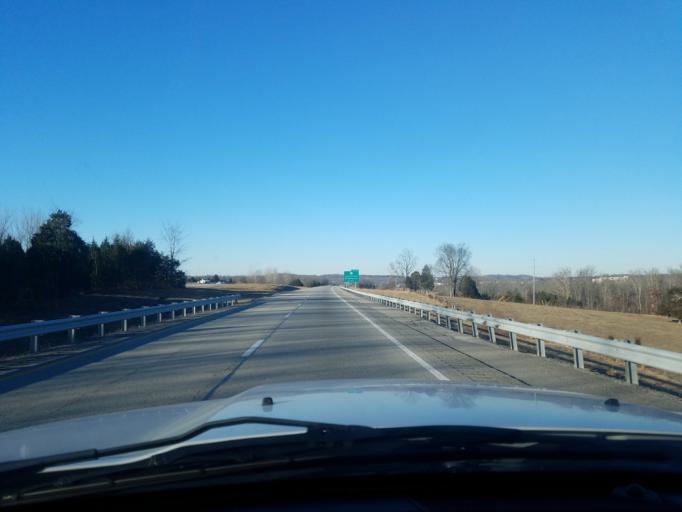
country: US
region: Kentucky
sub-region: Grayson County
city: Leitchfield
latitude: 37.4685
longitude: -86.2721
